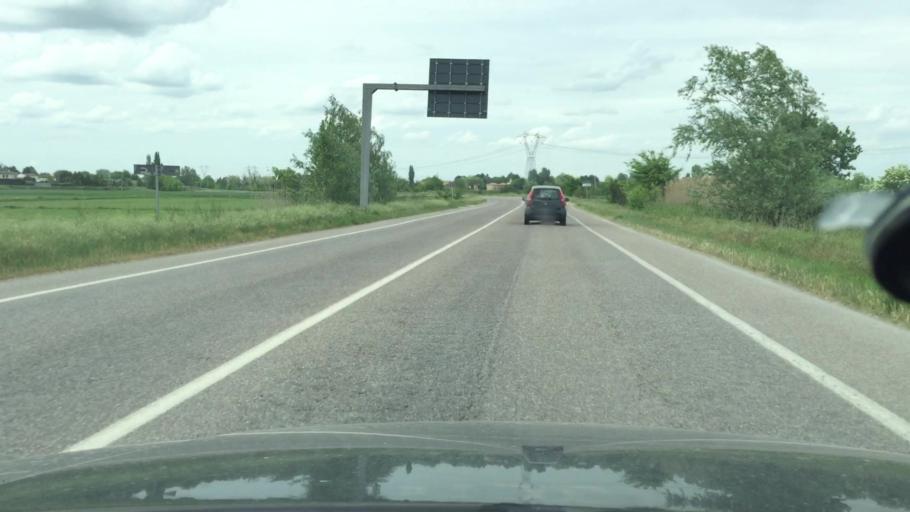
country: IT
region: Emilia-Romagna
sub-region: Provincia di Ferrara
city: Cona
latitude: 44.8073
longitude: 11.7190
